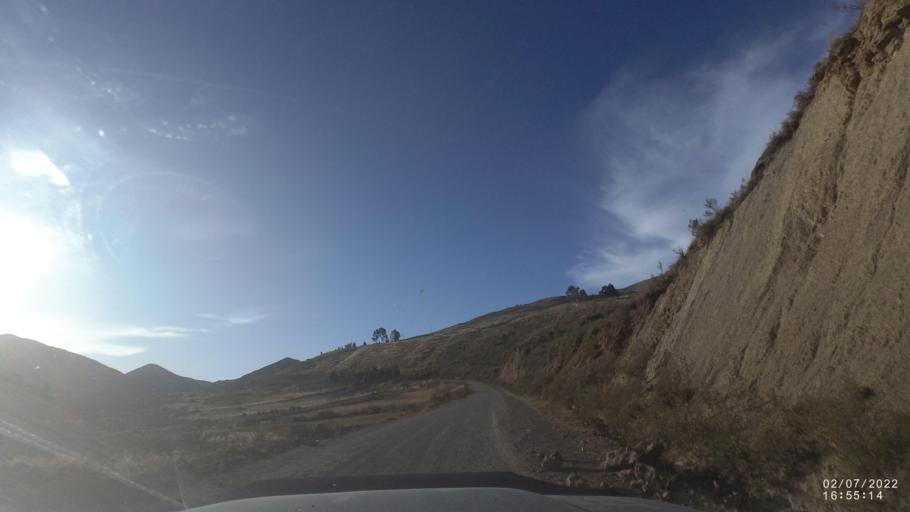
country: BO
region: Cochabamba
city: Irpa Irpa
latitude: -17.9620
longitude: -66.5407
